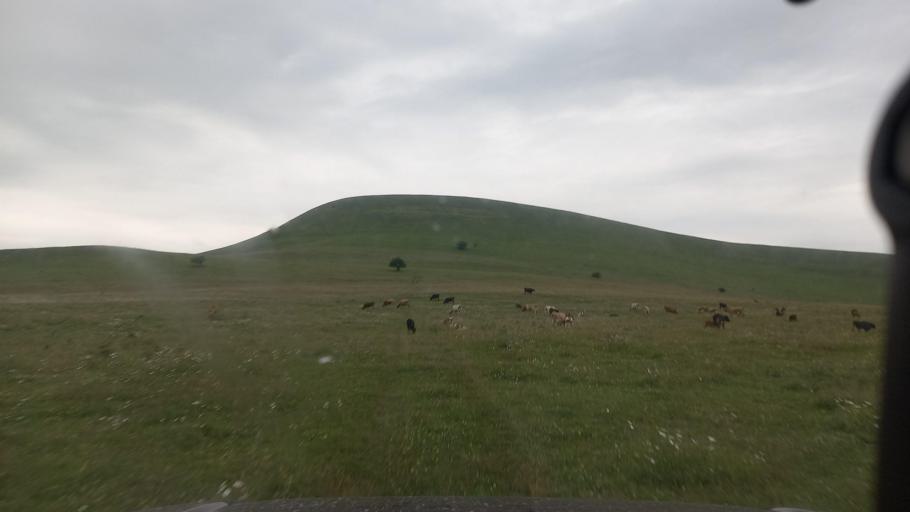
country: RU
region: Karachayevo-Cherkesiya
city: Pregradnaya
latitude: 43.9508
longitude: 41.1612
